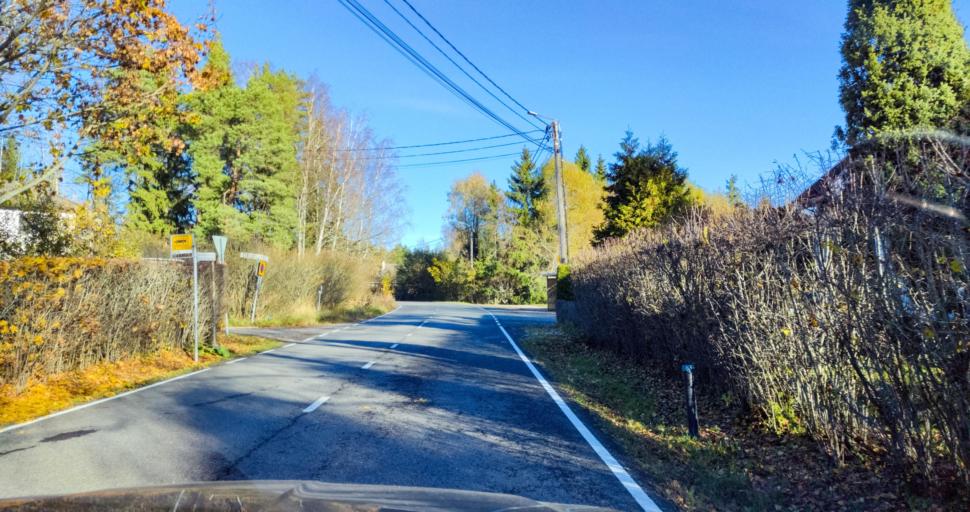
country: FI
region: Varsinais-Suomi
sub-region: Turku
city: Turku
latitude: 60.3963
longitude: 22.2056
